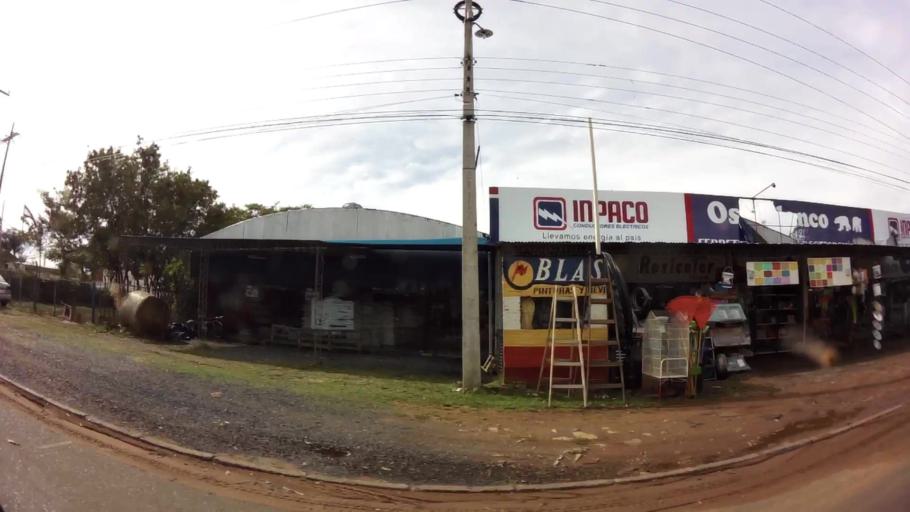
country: PY
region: Central
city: Limpio
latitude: -25.1663
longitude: -57.4691
